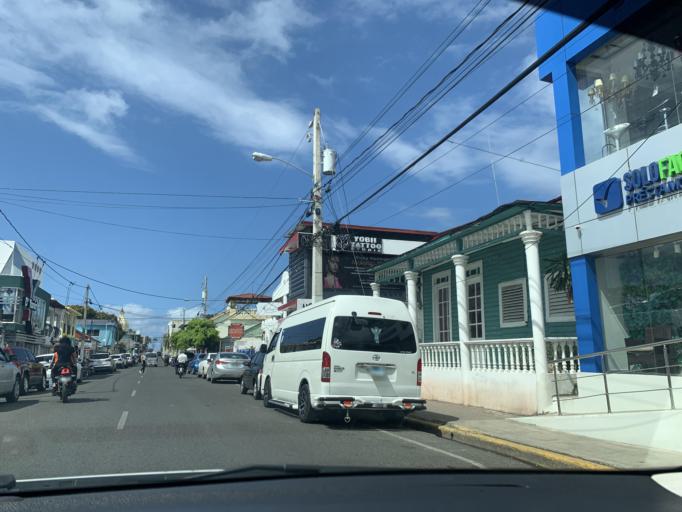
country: DO
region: Puerto Plata
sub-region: Puerto Plata
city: Puerto Plata
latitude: 19.7948
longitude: -70.6949
